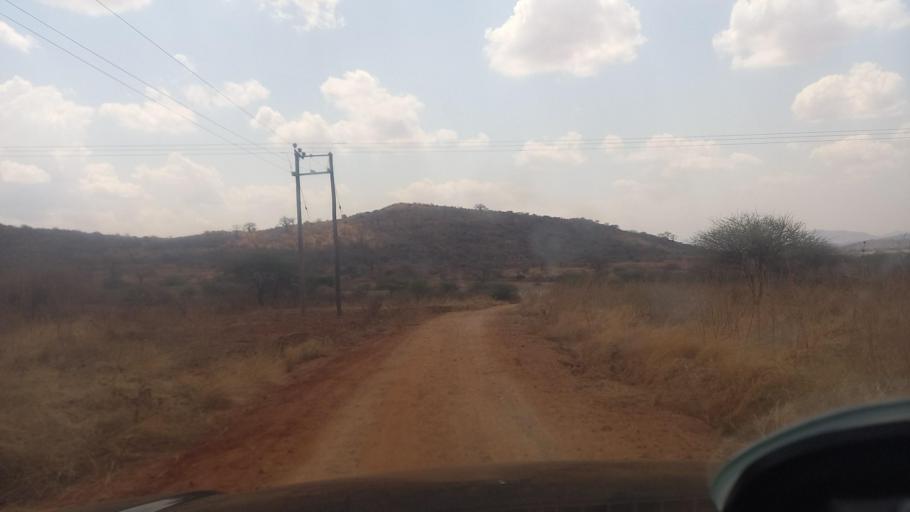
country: TZ
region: Dodoma
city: Kongwa
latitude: -6.1223
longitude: 36.2495
